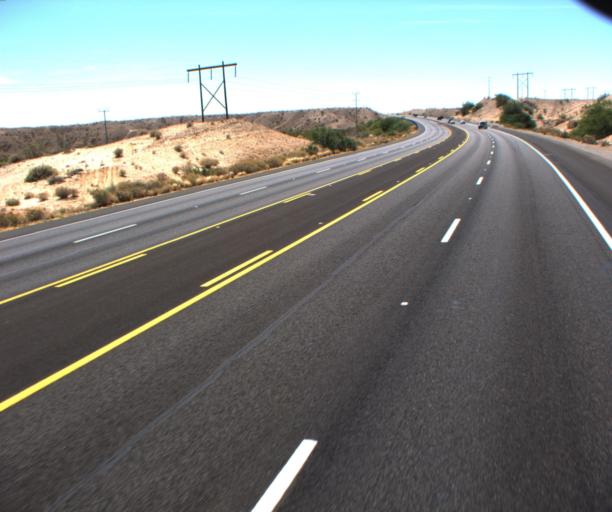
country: US
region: Arizona
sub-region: La Paz County
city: Cienega Springs
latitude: 34.1750
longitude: -114.2459
